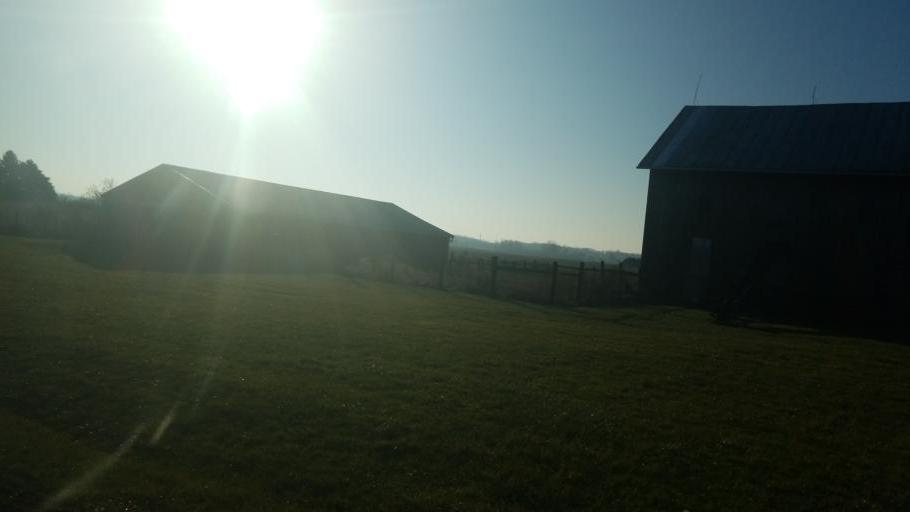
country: US
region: Ohio
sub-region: Crawford County
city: Bucyrus
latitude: 40.8374
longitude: -82.9528
